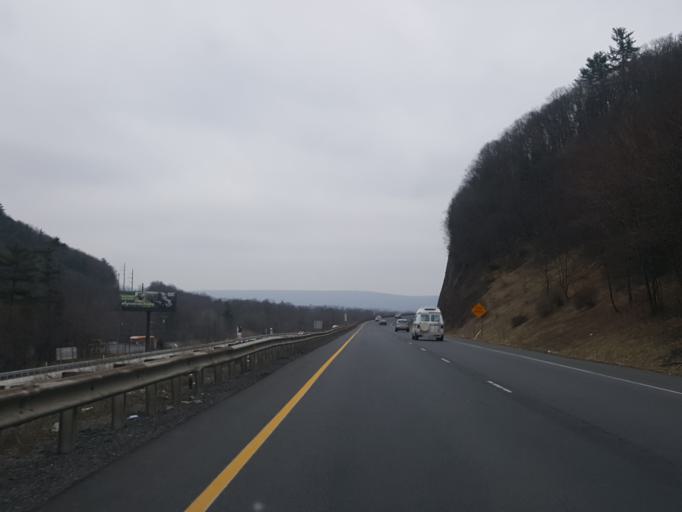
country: US
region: Pennsylvania
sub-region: Schuylkill County
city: Pine Grove
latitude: 40.5836
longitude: -76.4086
